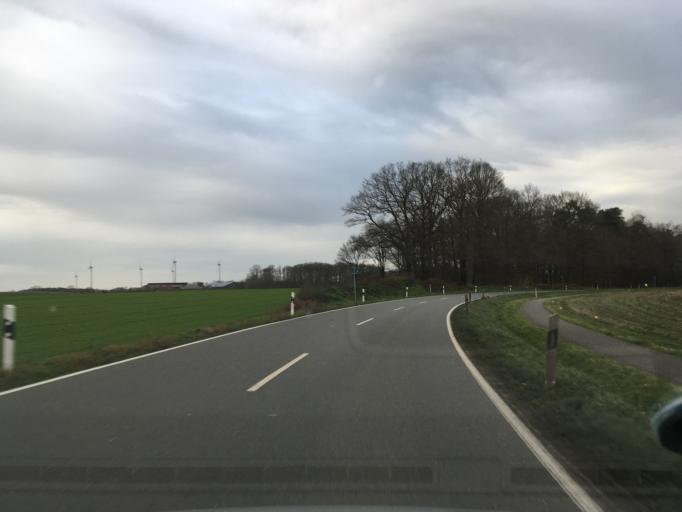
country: DE
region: North Rhine-Westphalia
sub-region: Regierungsbezirk Munster
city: Schoppingen
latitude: 52.0893
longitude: 7.2125
